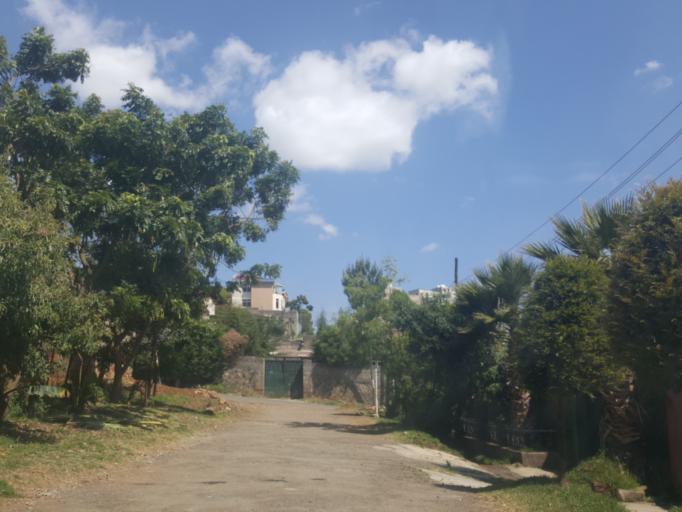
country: ET
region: Adis Abeba
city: Addis Ababa
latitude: 9.0560
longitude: 38.7362
